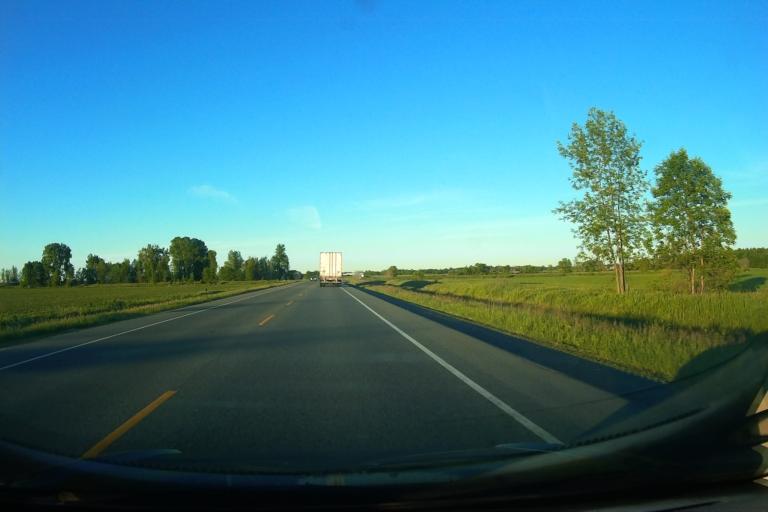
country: CA
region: Ontario
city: Prescott
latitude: 45.0555
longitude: -75.4614
